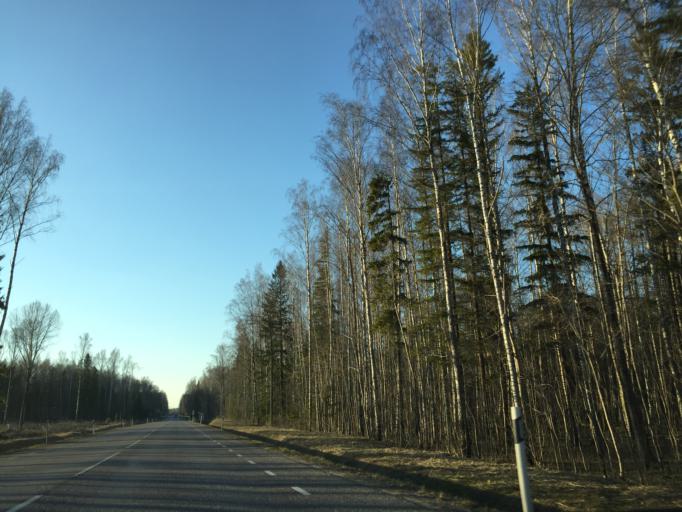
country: EE
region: Ida-Virumaa
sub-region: Johvi vald
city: Johvi
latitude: 59.3220
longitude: 27.4890
